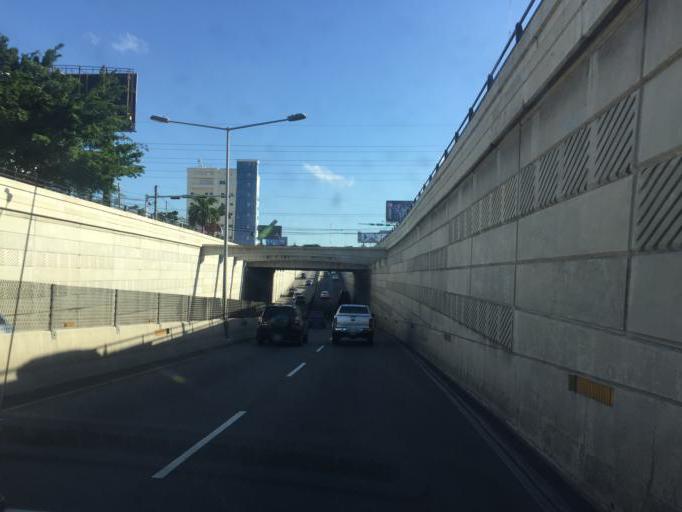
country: DO
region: Nacional
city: Bella Vista
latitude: 18.4543
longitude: -69.9553
